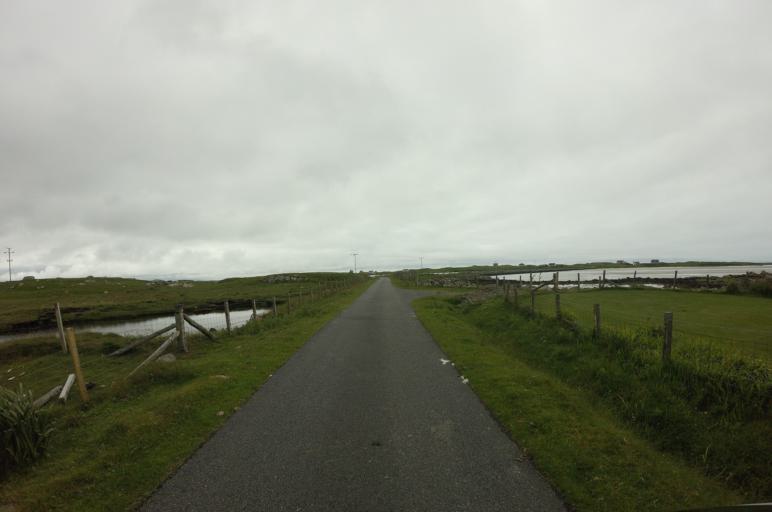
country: GB
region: Scotland
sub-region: Eilean Siar
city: Isle of North Uist
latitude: 57.5431
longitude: -7.3438
